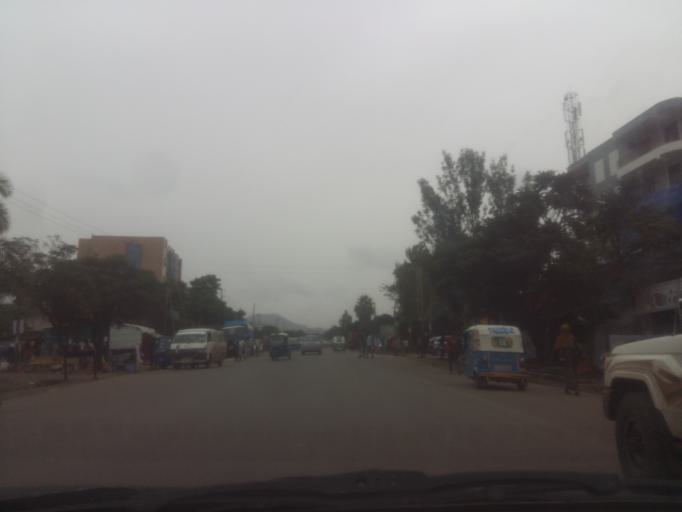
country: ET
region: Oromiya
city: Bishoftu
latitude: 8.7928
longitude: 38.9035
